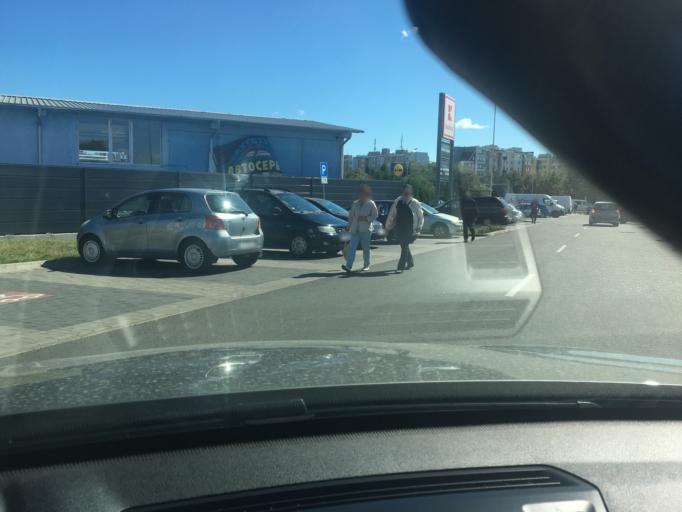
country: BG
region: Burgas
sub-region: Obshtina Burgas
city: Burgas
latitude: 42.5317
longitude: 27.4614
